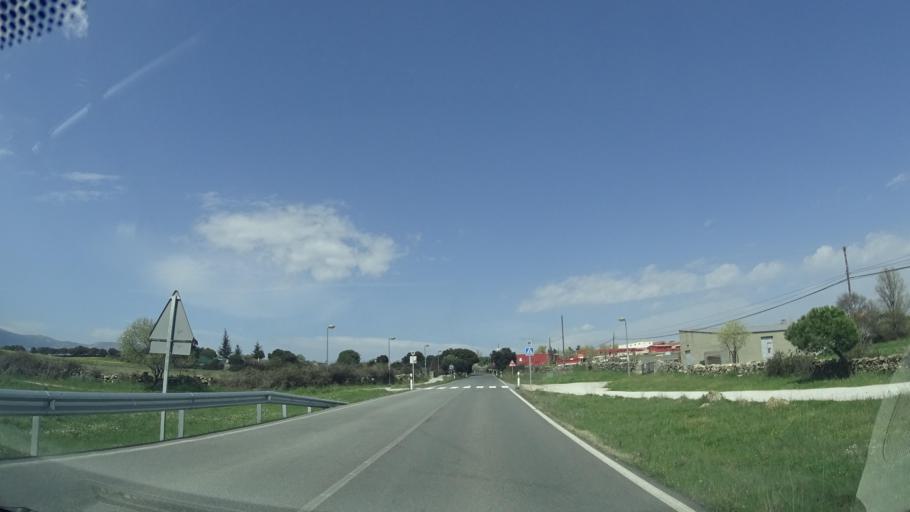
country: ES
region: Madrid
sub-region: Provincia de Madrid
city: Colmenar Viejo
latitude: 40.6915
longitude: -3.7695
